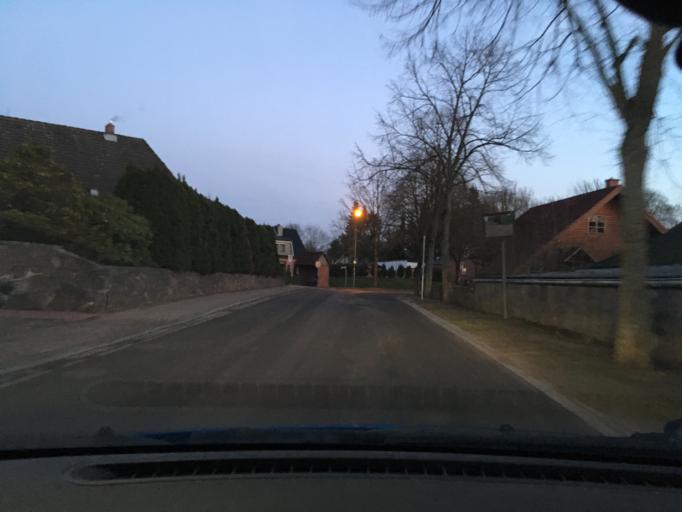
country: DE
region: Schleswig-Holstein
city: Fitzen
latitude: 53.4822
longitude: 10.6382
